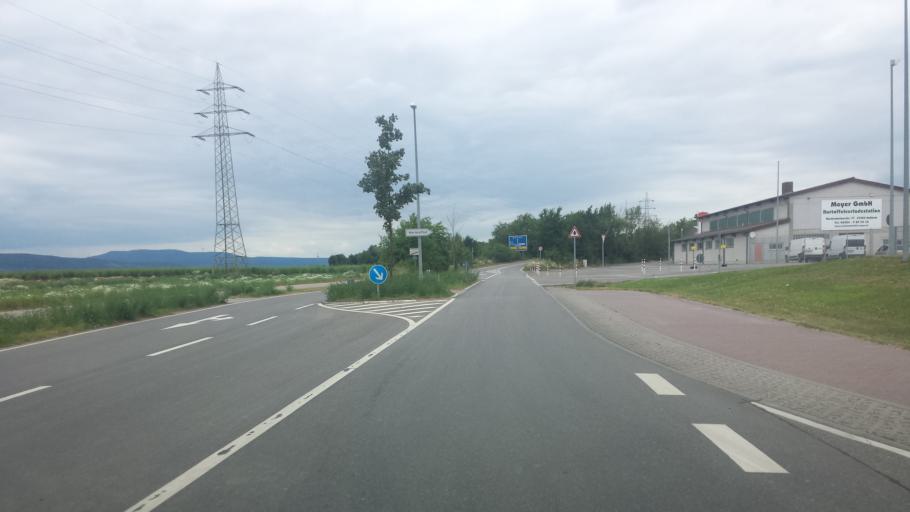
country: DE
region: Rheinland-Pfalz
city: Hassloch
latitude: 49.3784
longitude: 8.2511
